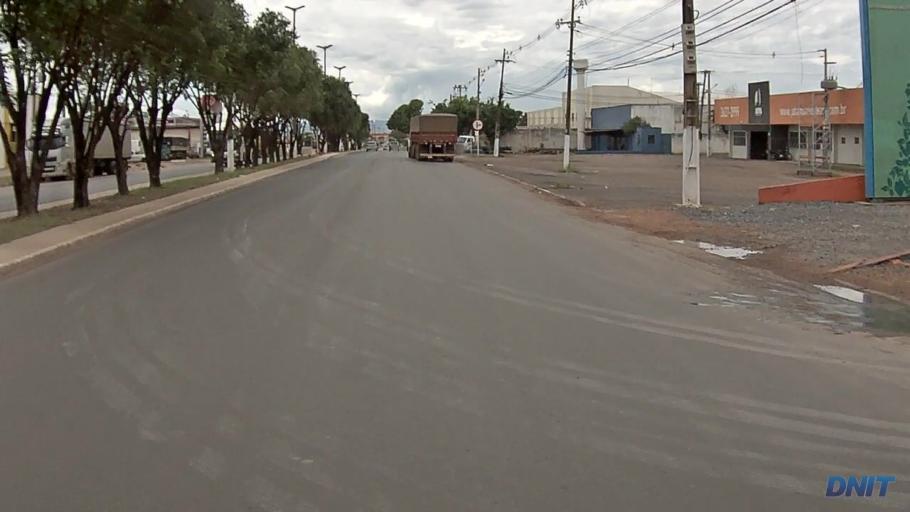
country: BR
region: Mato Grosso
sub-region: Varzea Grande
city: Varzea Grande
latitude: -15.6452
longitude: -56.1849
